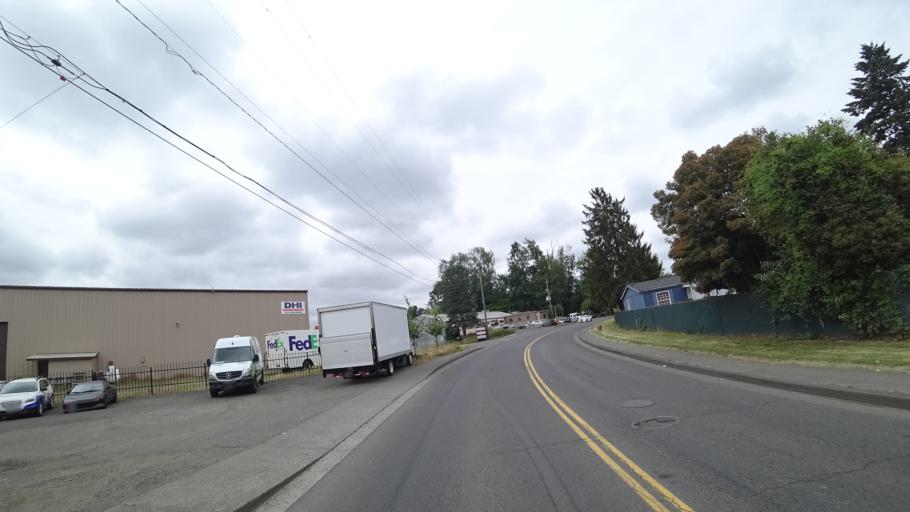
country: US
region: Washington
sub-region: Clark County
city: Vancouver
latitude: 45.5879
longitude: -122.6619
